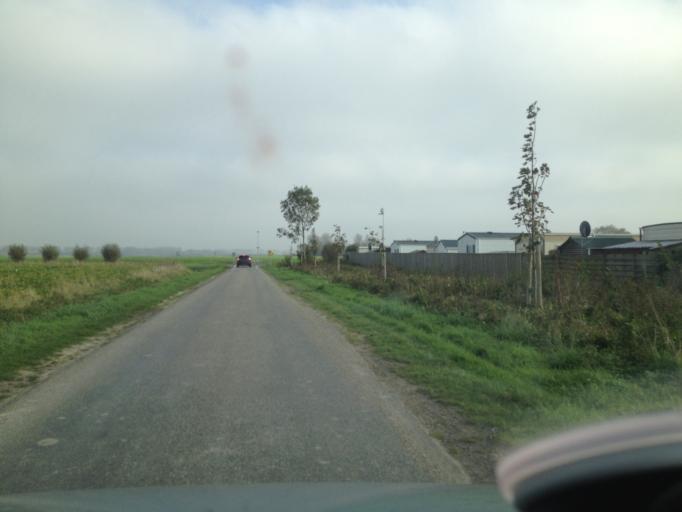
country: NL
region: Zeeland
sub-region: Gemeente Vlissingen
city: Vlissingen
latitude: 51.3842
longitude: 3.5161
